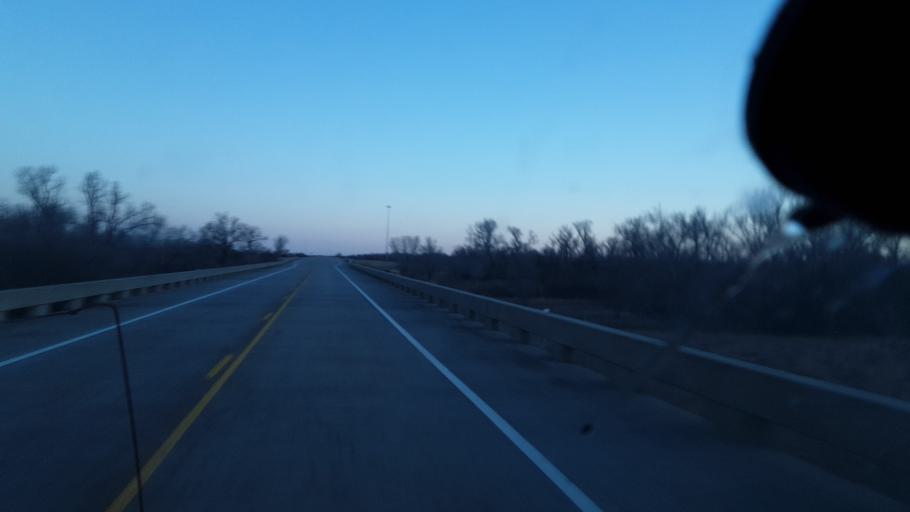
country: US
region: Kansas
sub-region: Reno County
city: South Hutchinson
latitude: 38.0505
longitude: -97.9858
